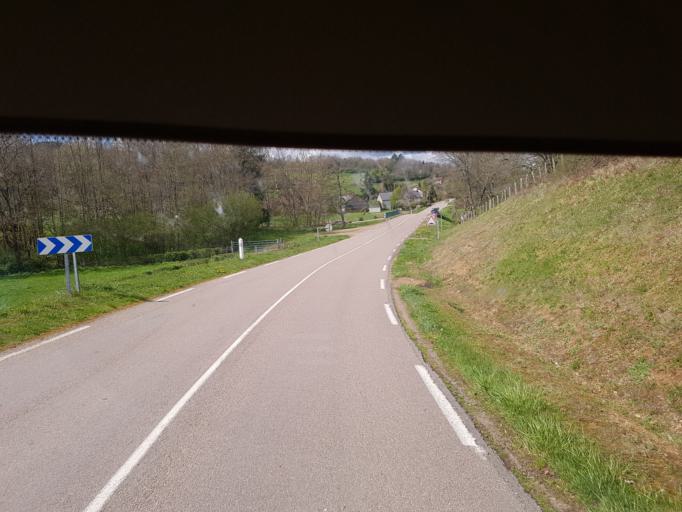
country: FR
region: Bourgogne
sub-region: Departement de Saone-et-Loire
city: Autun
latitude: 47.0978
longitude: 4.2319
